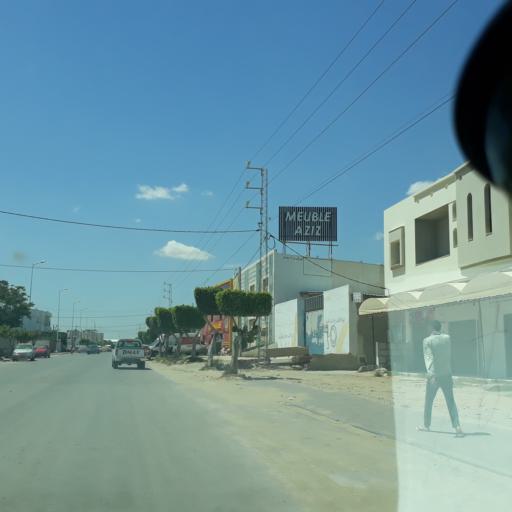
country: TN
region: Safaqis
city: Sfax
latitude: 34.8151
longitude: 10.7395
